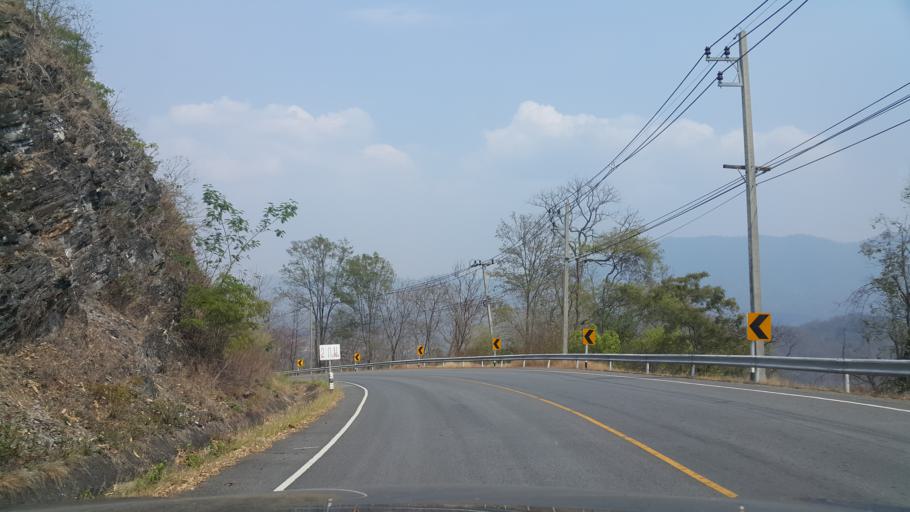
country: TH
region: Lamphun
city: Thung Hua Chang
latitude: 17.9072
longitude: 99.1476
